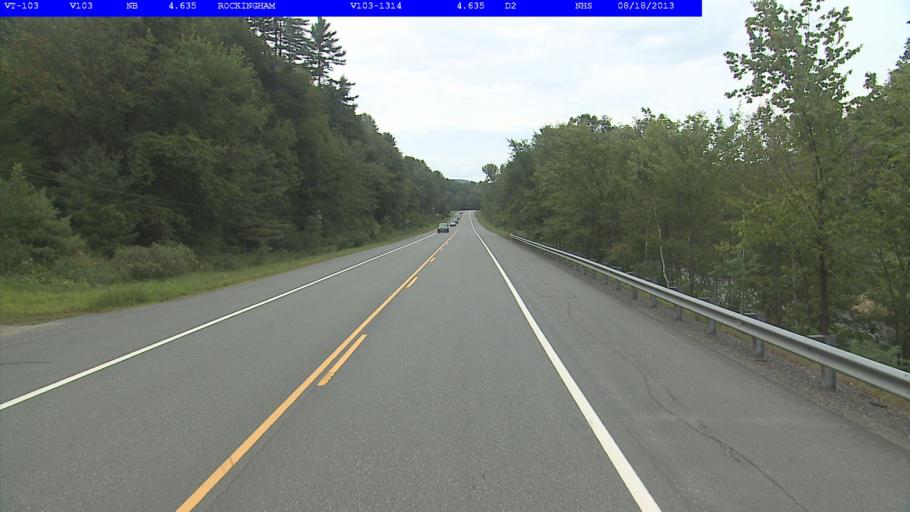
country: US
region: Vermont
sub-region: Windham County
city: Rockingham
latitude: 43.2085
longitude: -72.5375
